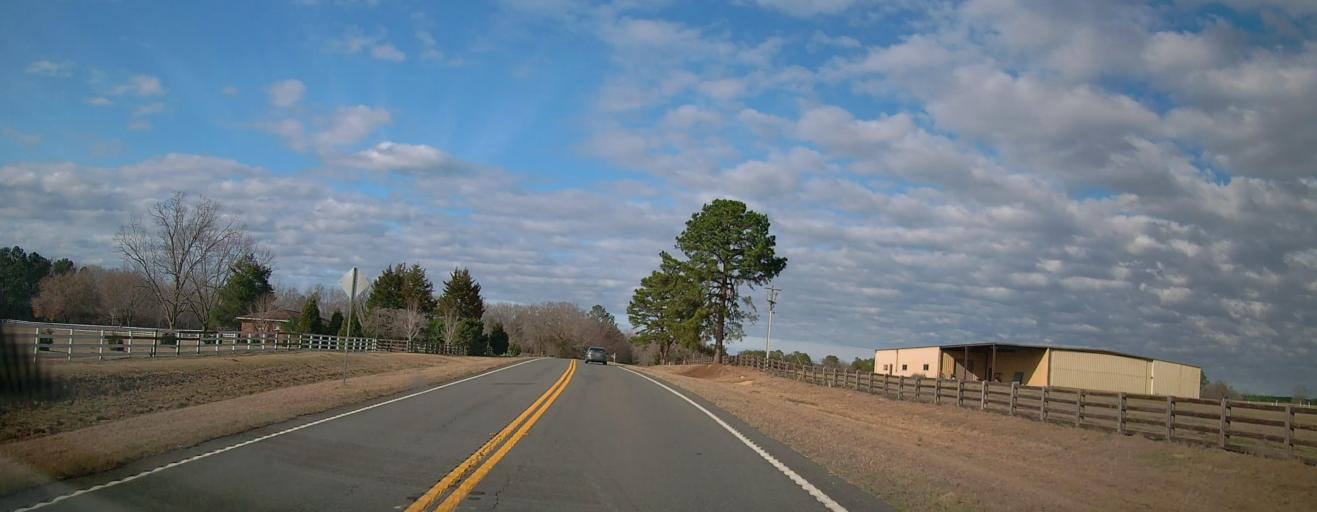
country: US
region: Georgia
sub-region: Talbot County
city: Talbotton
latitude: 32.5366
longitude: -84.6032
